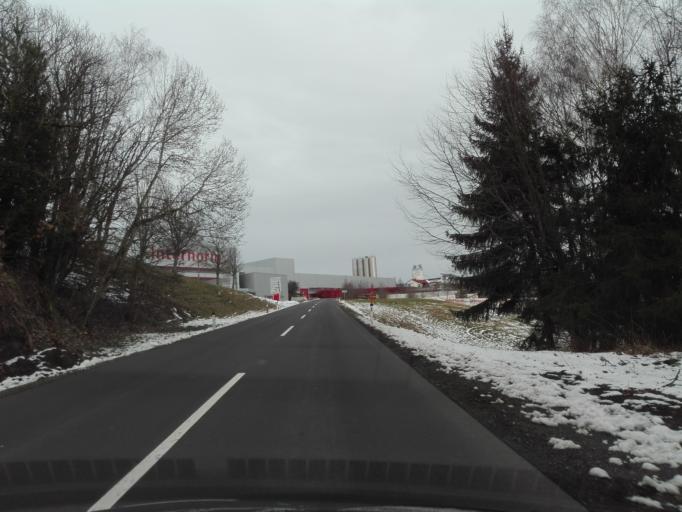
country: AT
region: Upper Austria
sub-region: Politischer Bezirk Rohrbach
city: Atzesberg
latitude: 48.5472
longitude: 13.8923
